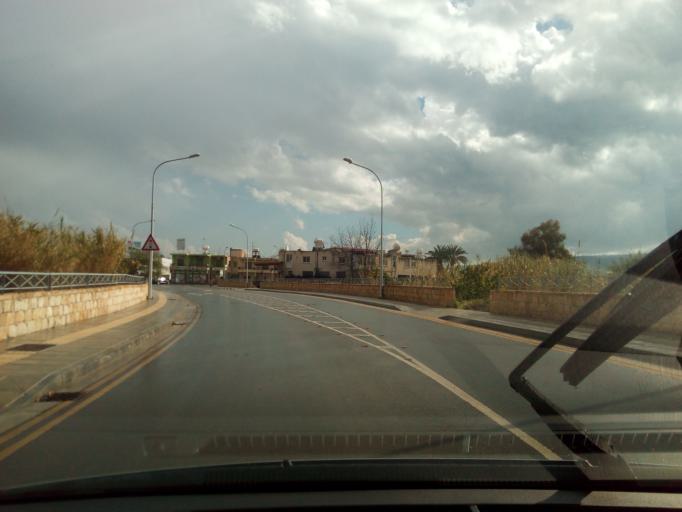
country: CY
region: Pafos
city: Polis
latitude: 35.0326
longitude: 32.4229
